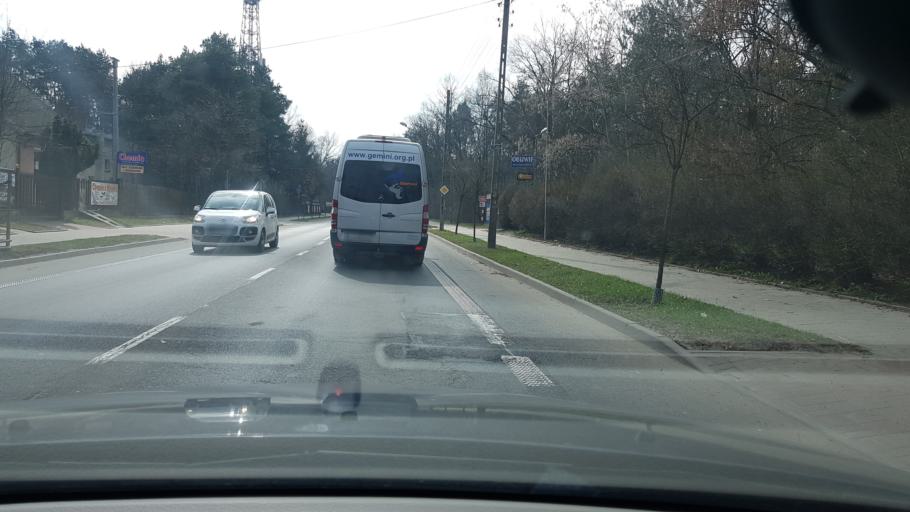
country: PL
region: Masovian Voivodeship
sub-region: Warszawa
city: Wesola
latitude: 52.2501
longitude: 21.2237
